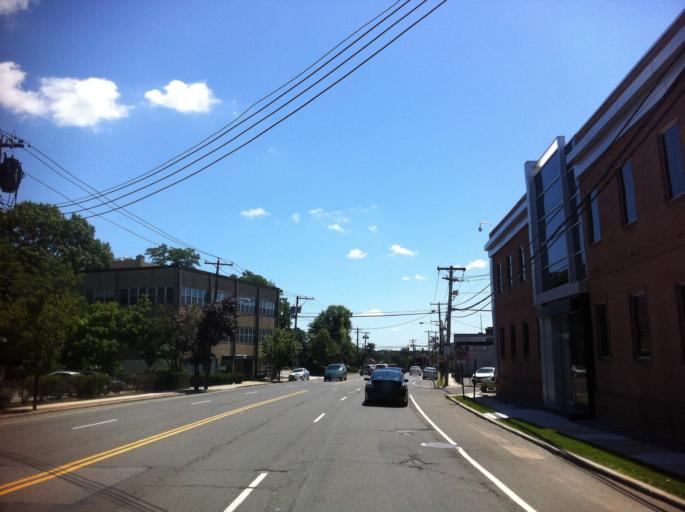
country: US
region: New York
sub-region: Nassau County
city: Roslyn Heights
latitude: 40.7889
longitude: -73.6516
